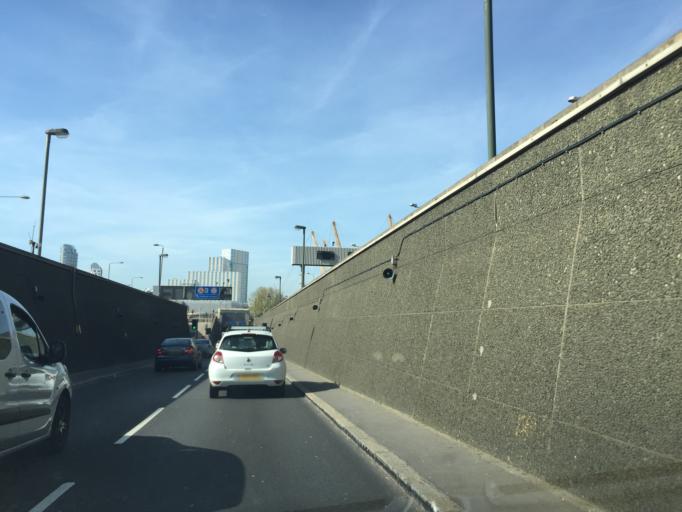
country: GB
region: England
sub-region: Greater London
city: Poplar
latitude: 51.4972
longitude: 0.0019
